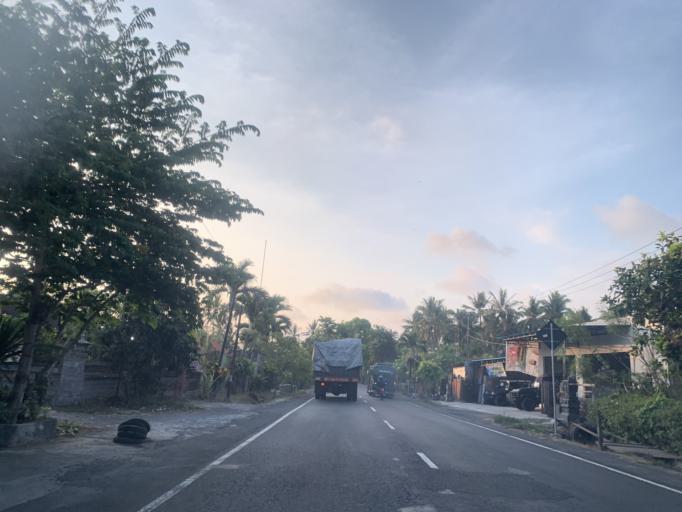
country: ID
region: Bali
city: Banjar Swastika
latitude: -8.4331
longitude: 114.8554
